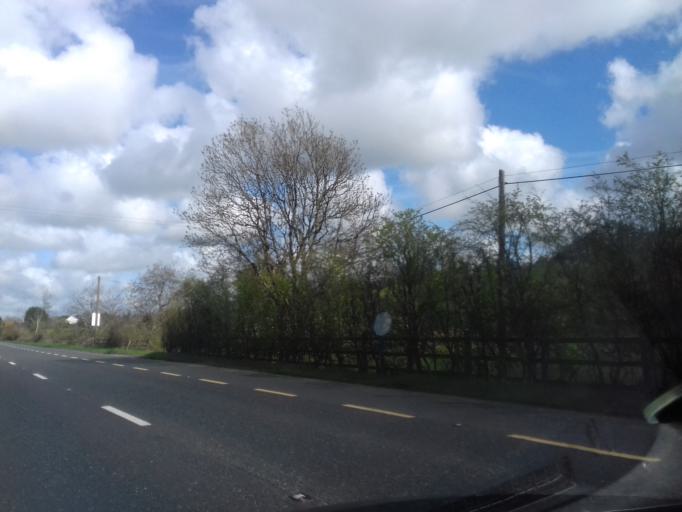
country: IE
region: Ulster
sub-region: An Cabhan
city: Ballyjamesduff
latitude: 53.9151
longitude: -7.2048
